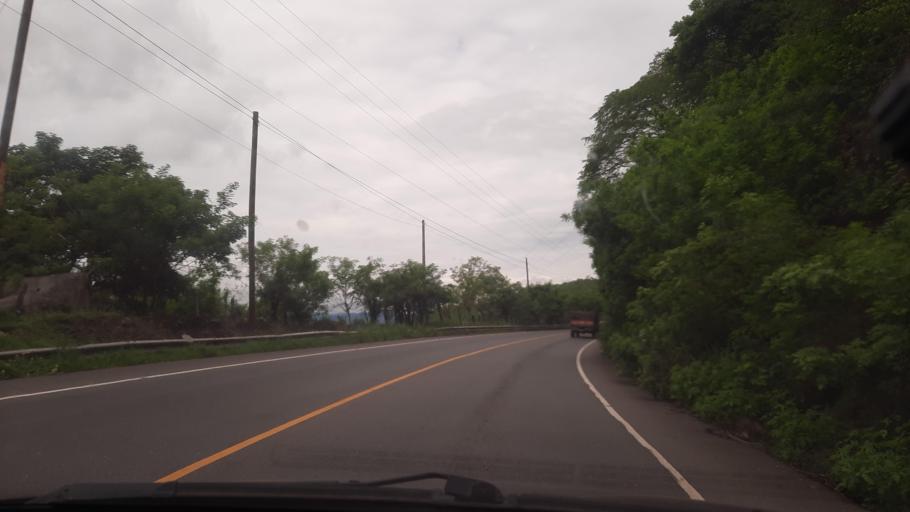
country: GT
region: Zacapa
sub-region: Municipio de Zacapa
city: Gualan
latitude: 15.1609
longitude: -89.3165
